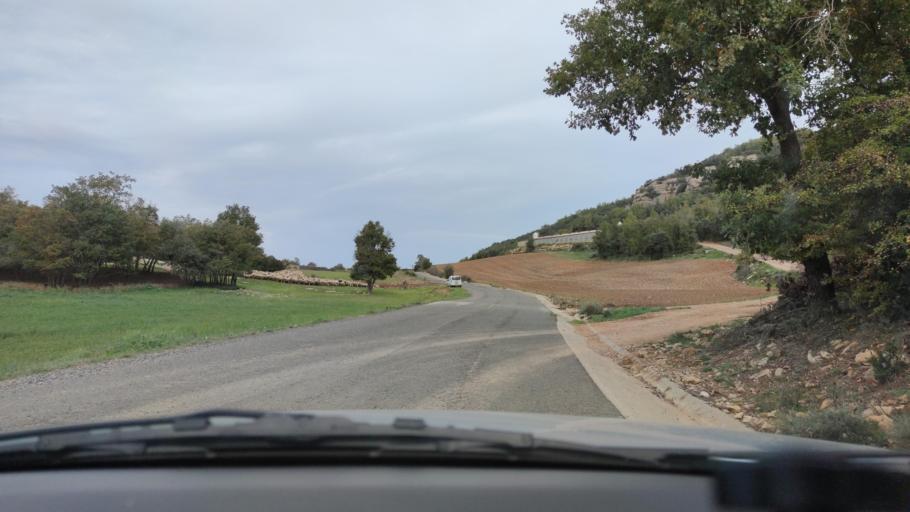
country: ES
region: Catalonia
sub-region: Provincia de Lleida
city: Llimiana
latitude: 42.0360
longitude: 1.0061
